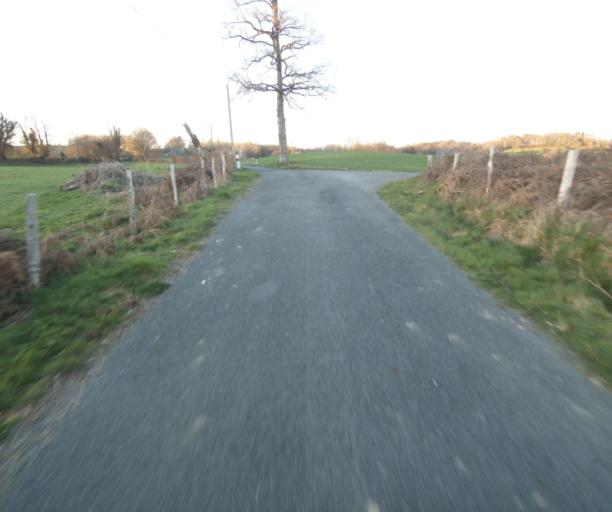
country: FR
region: Limousin
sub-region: Departement de la Correze
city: Saint-Clement
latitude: 45.3708
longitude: 1.6184
